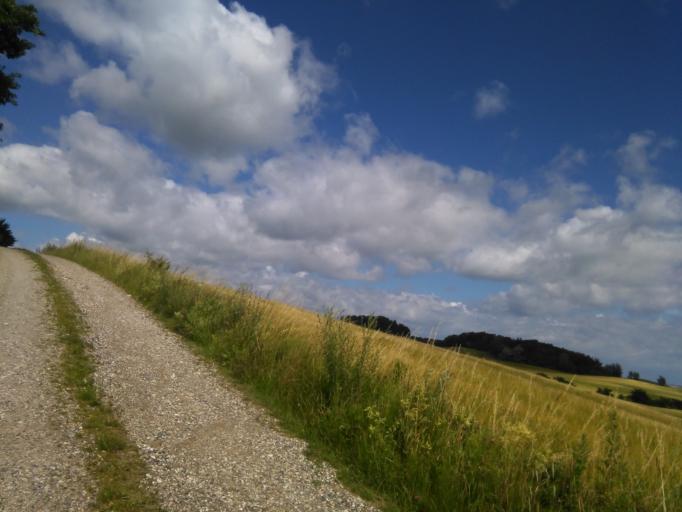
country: DK
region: Central Jutland
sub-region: Arhus Kommune
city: Logten
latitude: 56.1661
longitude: 10.3976
